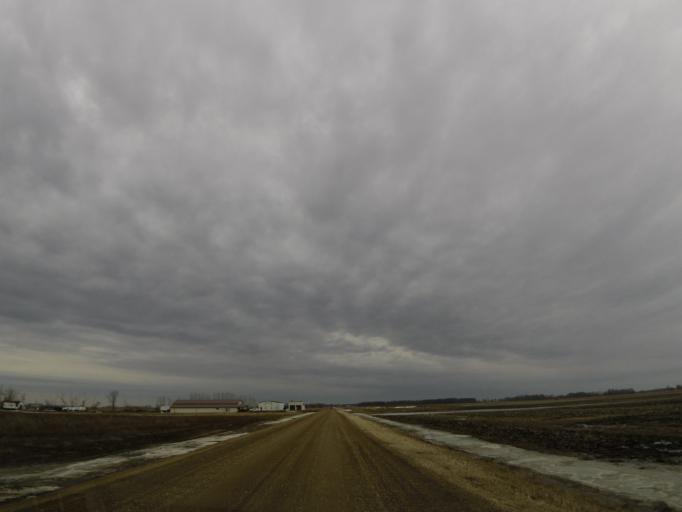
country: US
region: North Dakota
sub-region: Walsh County
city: Grafton
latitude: 48.4198
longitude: -97.4498
